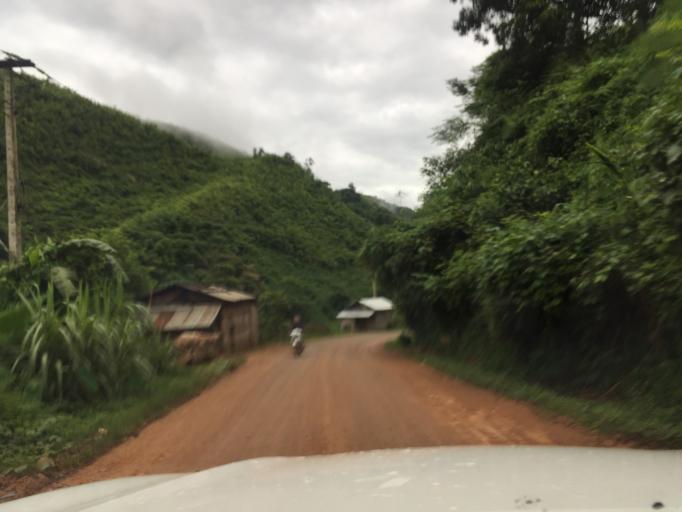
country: LA
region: Oudomxai
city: Muang La
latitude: 20.9581
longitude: 102.2184
